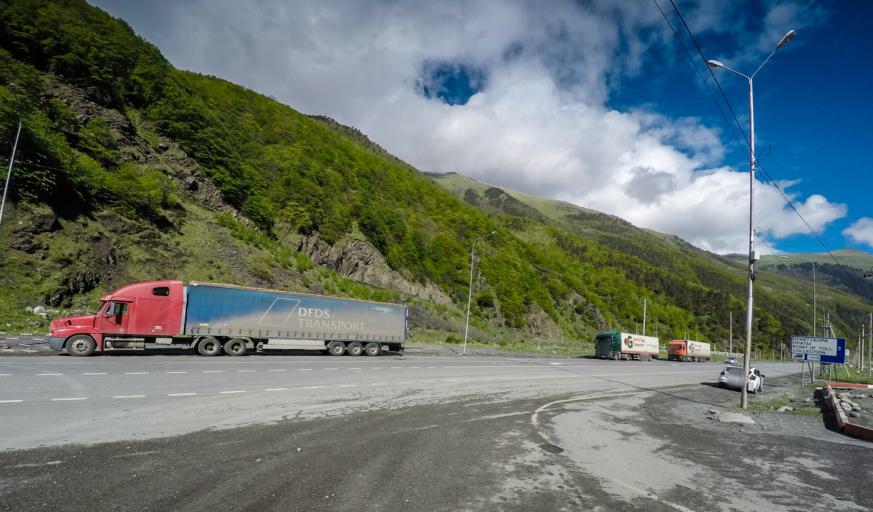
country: RU
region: Ingushetiya
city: Dzhayrakh
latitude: 42.7733
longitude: 44.6308
